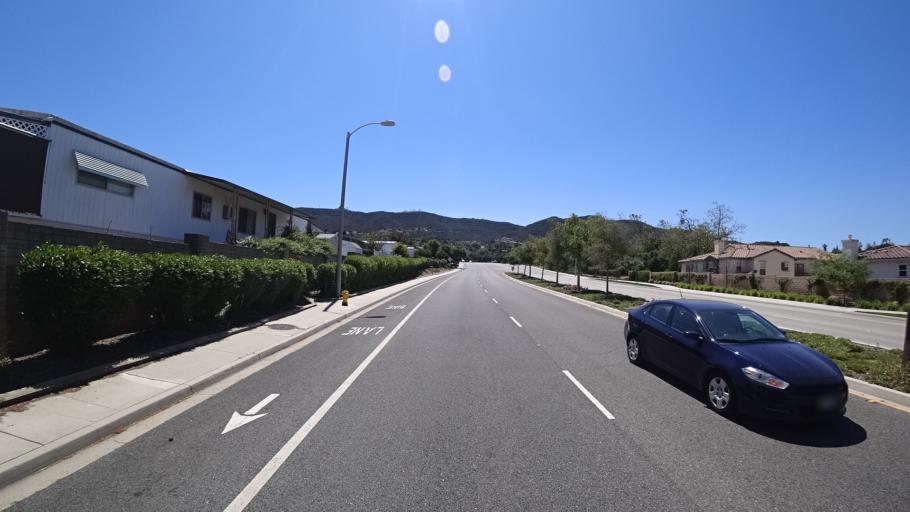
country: US
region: California
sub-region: Ventura County
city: Casa Conejo
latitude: 34.1795
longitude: -118.9111
